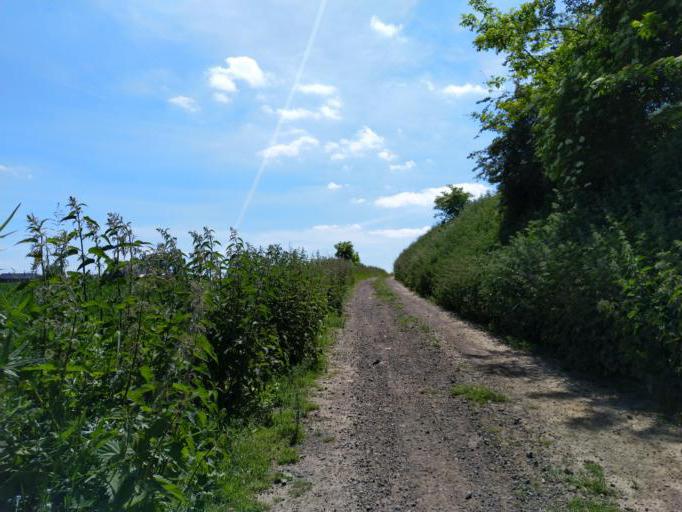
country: BE
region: Wallonia
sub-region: Province du Hainaut
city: Roeulx
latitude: 50.5004
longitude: 4.0746
